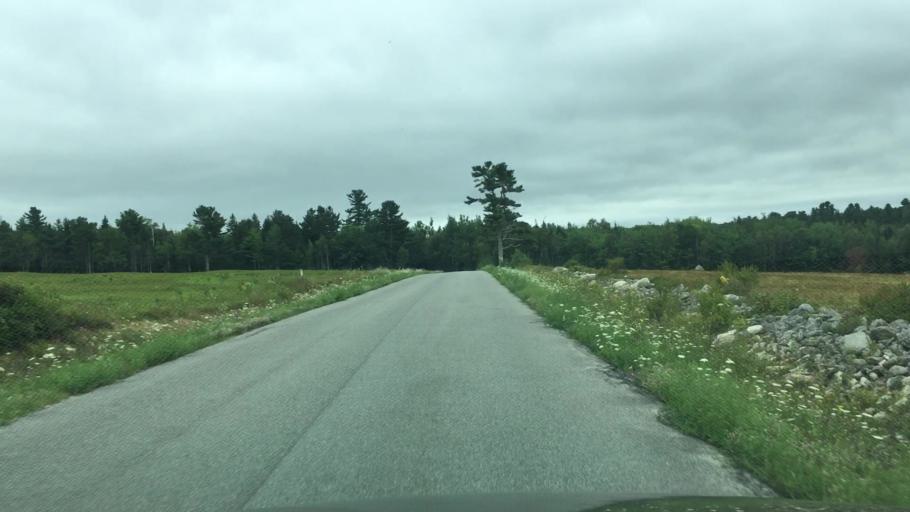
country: US
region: Maine
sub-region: Waldo County
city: Stockton Springs
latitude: 44.5236
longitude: -68.8815
